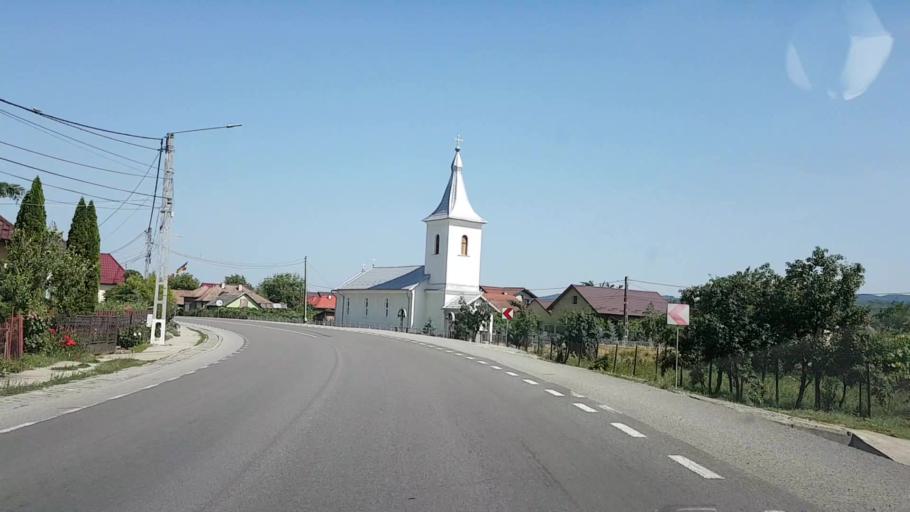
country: RO
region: Bistrita-Nasaud
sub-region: Comuna Uriu
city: Cristestii Ciceului
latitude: 47.1938
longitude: 24.0863
